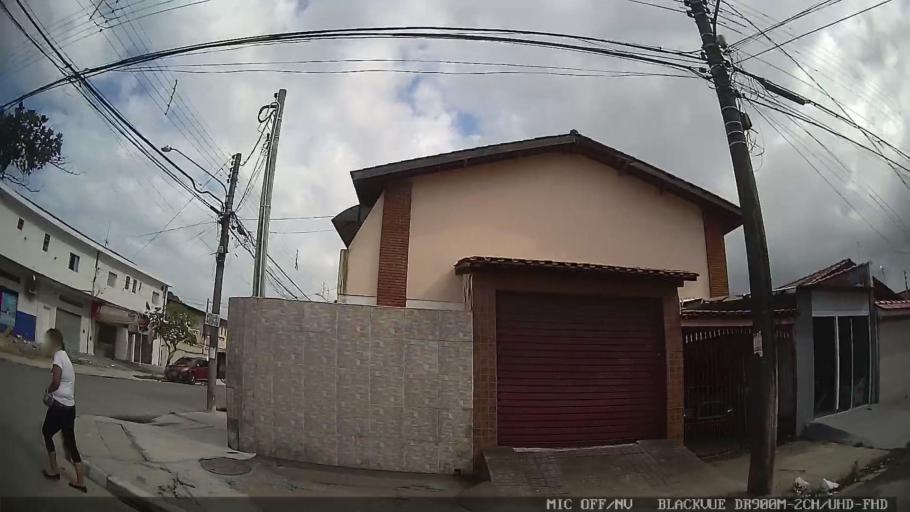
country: BR
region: Sao Paulo
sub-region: Guaruja
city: Guaruja
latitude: -23.9962
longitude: -46.2816
